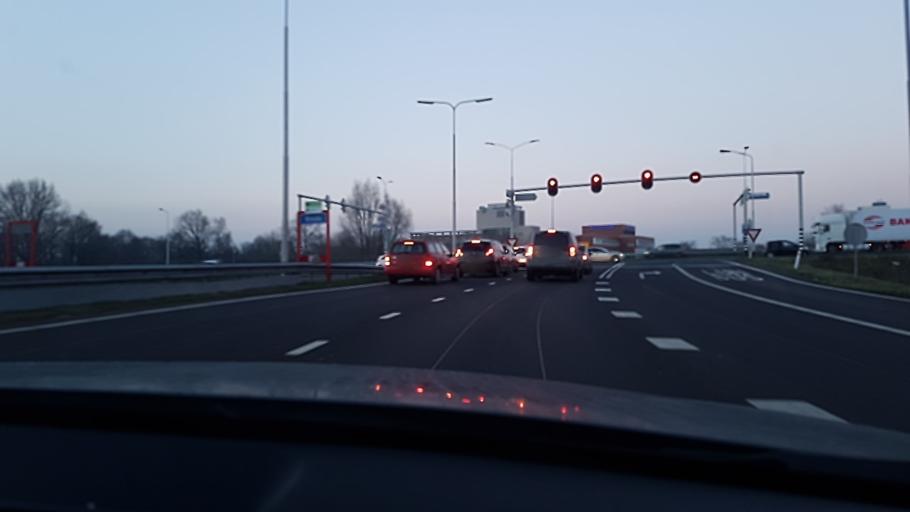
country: NL
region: North Brabant
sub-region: Gemeente Breda
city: Hoge Vucht
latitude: 51.5815
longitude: 4.8213
